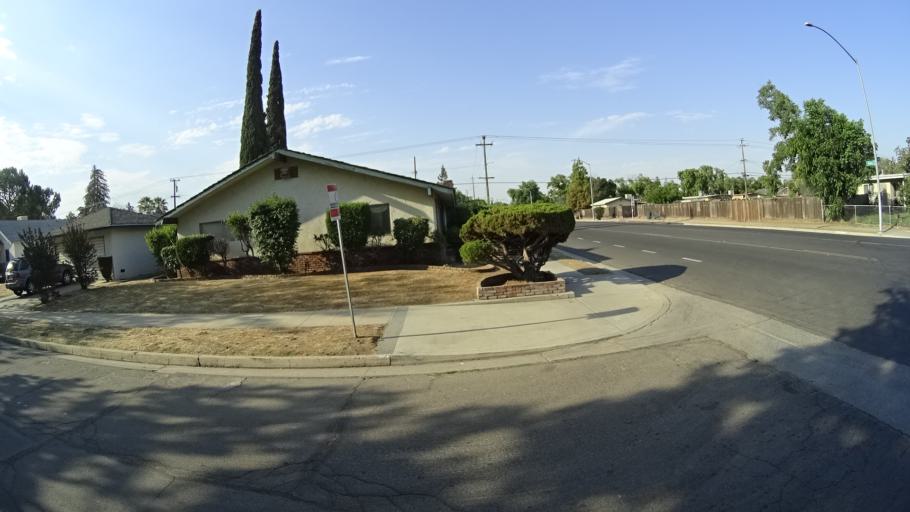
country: US
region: California
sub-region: Fresno County
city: West Park
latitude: 36.7254
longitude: -119.8130
